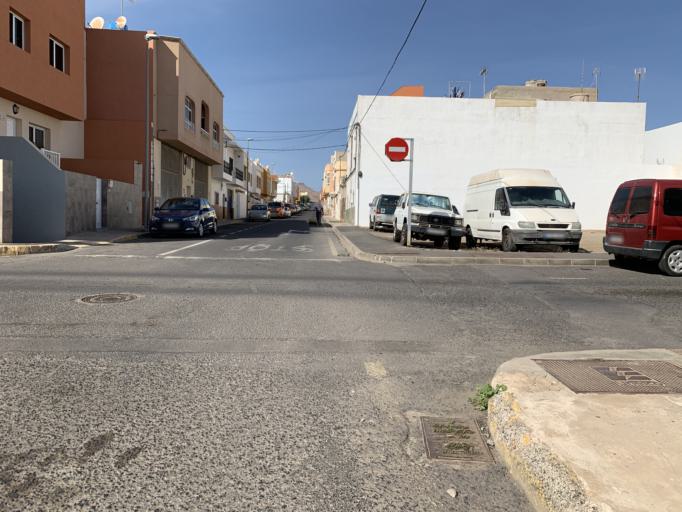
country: ES
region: Canary Islands
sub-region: Provincia de Las Palmas
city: Puerto del Rosario
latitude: 28.4991
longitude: -13.8674
